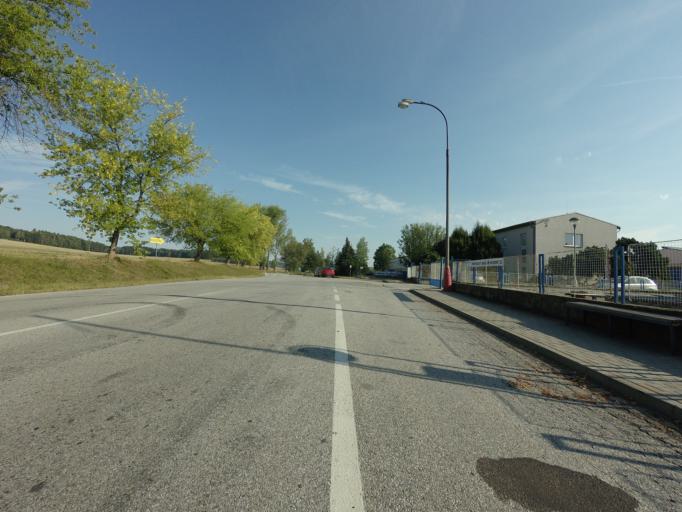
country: CZ
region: Jihocesky
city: Tyn nad Vltavou
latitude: 49.2325
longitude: 14.4215
